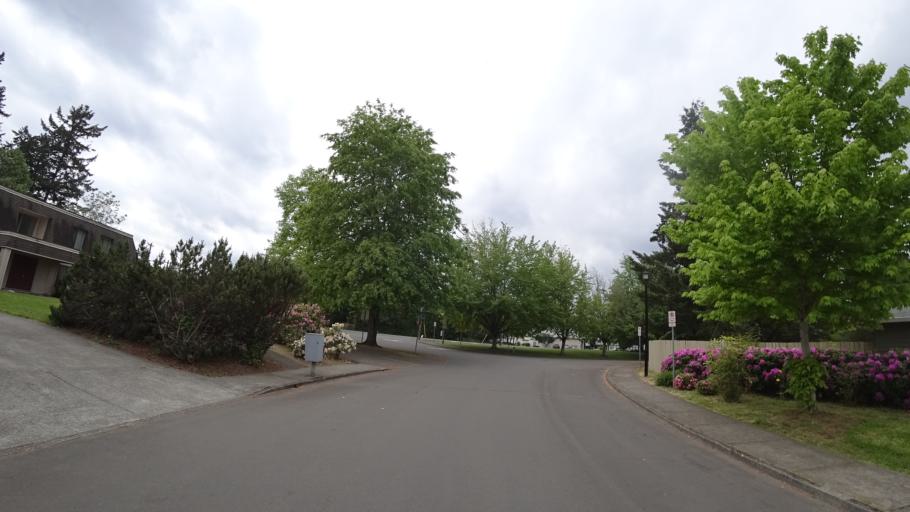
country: US
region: Oregon
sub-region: Washington County
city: Garden Home-Whitford
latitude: 45.4643
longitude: -122.7776
